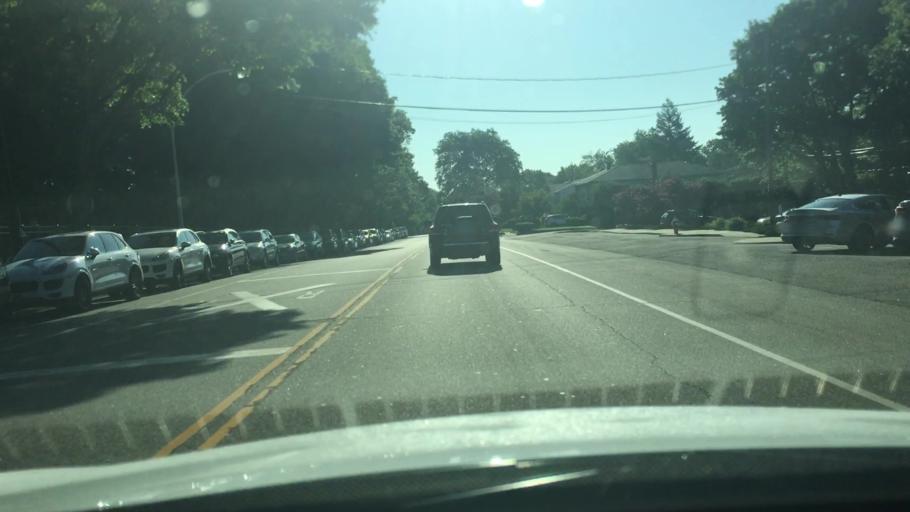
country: US
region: New York
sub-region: Nassau County
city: Albertson
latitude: 40.7711
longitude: -73.6406
